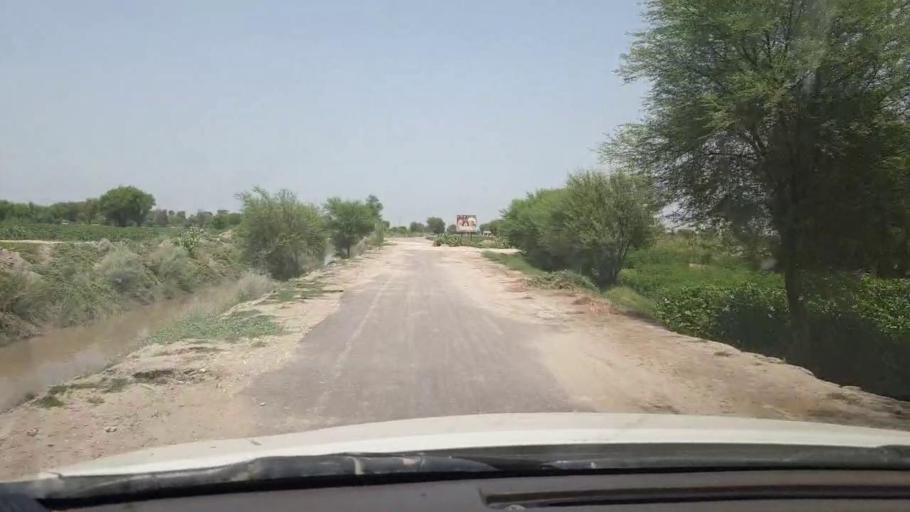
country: PK
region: Sindh
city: Rohri
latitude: 27.5231
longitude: 69.1781
